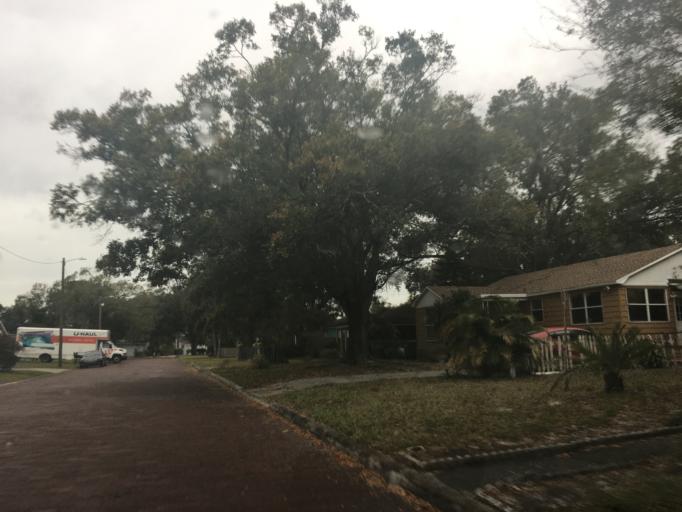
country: US
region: Florida
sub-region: Hillsborough County
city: Tampa
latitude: 27.9807
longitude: -82.4727
